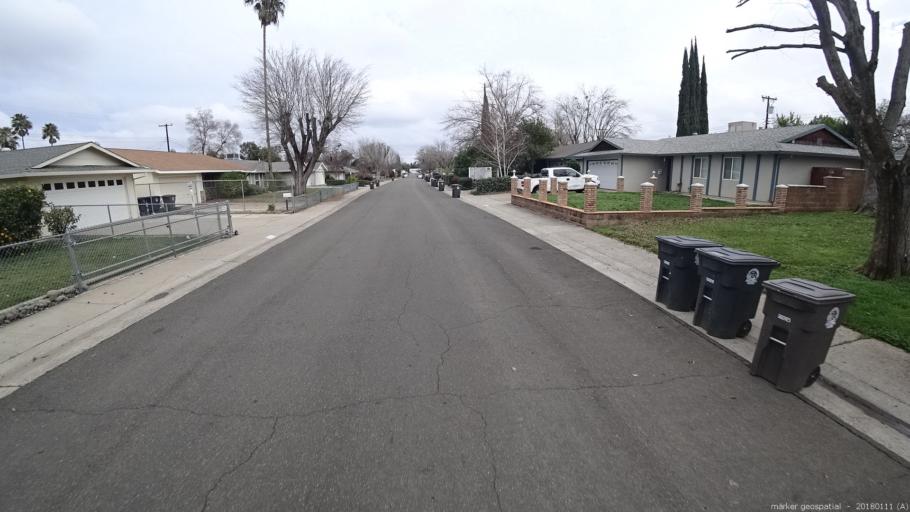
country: US
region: California
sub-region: Sacramento County
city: Rancho Cordova
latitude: 38.6169
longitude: -121.2878
